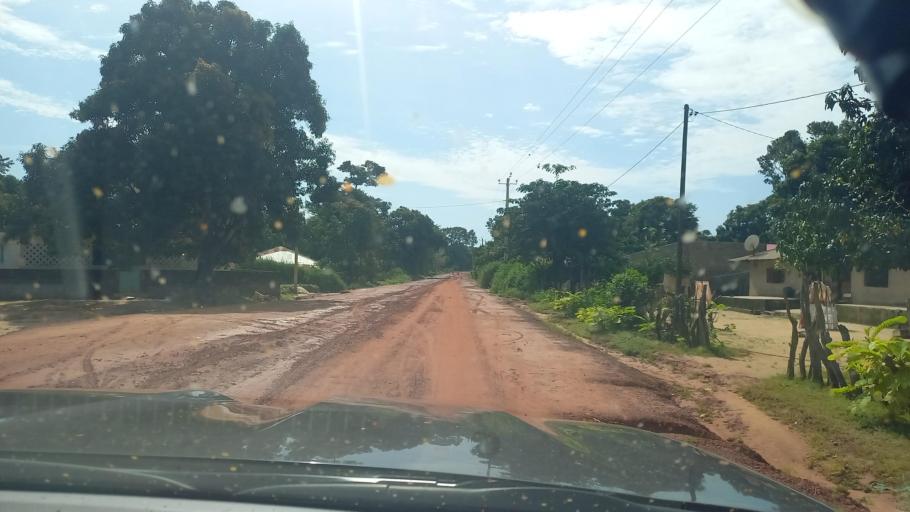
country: SN
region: Ziguinchor
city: Ziguinchor
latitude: 12.6744
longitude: -16.1935
